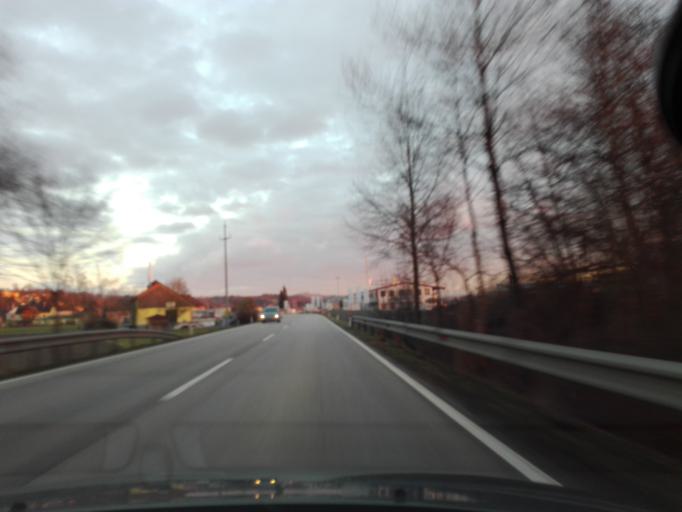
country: AT
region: Upper Austria
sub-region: Politischer Bezirk Perg
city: Bad Kreuzen
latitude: 48.2079
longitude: 14.7850
